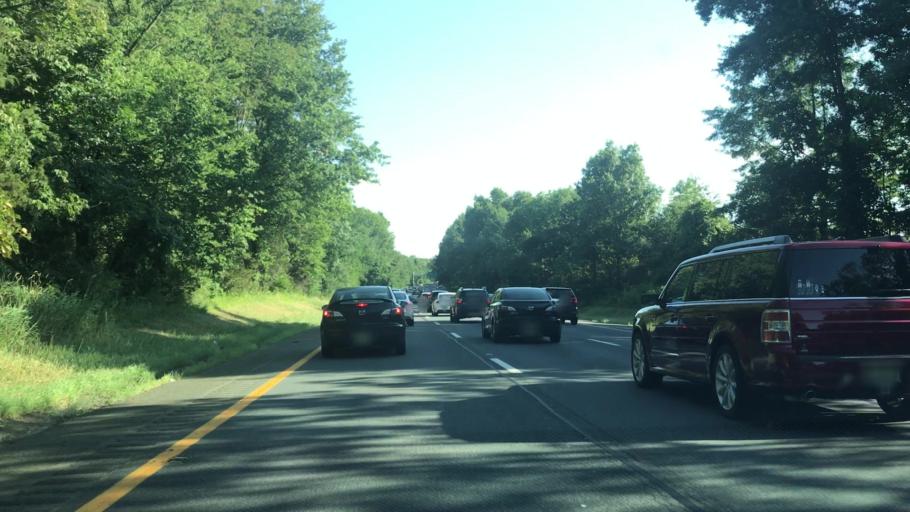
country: US
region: New Jersey
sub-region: Somerset County
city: Bernardsville
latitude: 40.7365
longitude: -74.5365
